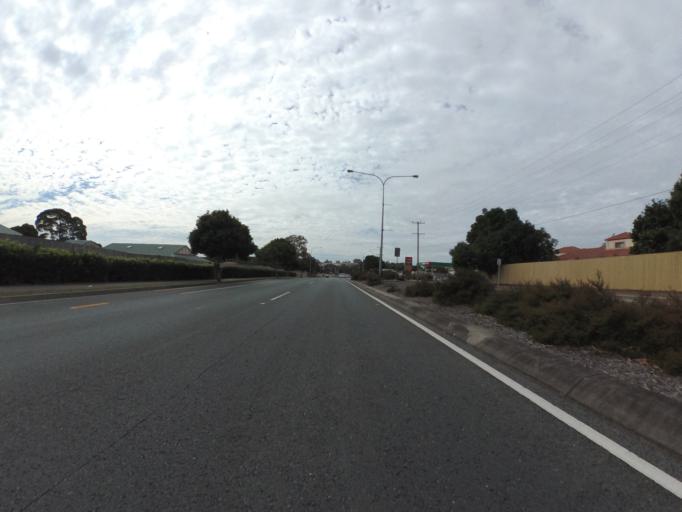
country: AU
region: Queensland
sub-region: Brisbane
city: Wynnum West
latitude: -27.4596
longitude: 153.1505
